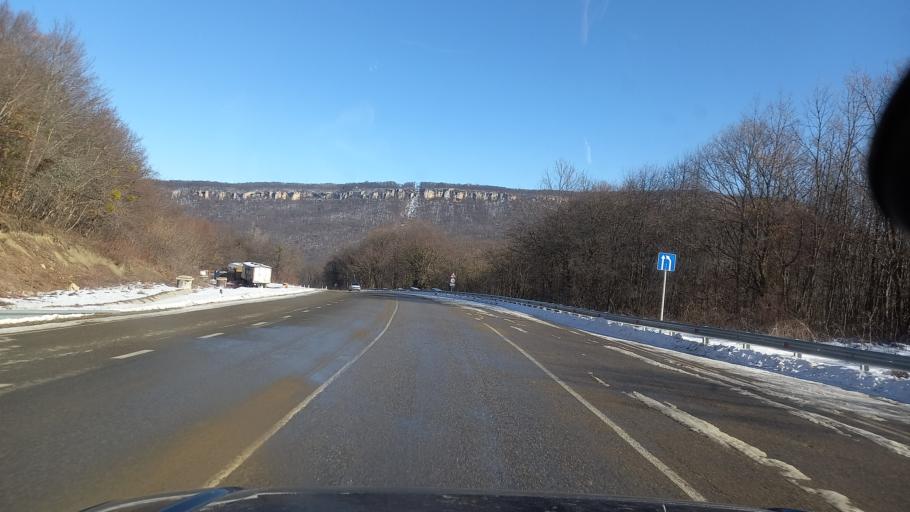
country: RU
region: Adygeya
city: Kamennomostskiy
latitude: 44.2436
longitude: 40.1870
